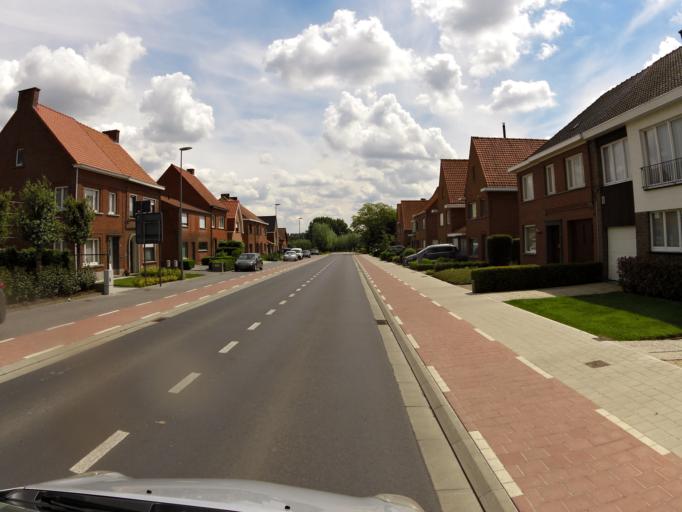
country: BE
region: Flanders
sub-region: Provincie West-Vlaanderen
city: Ieper
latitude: 50.8643
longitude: 2.9047
